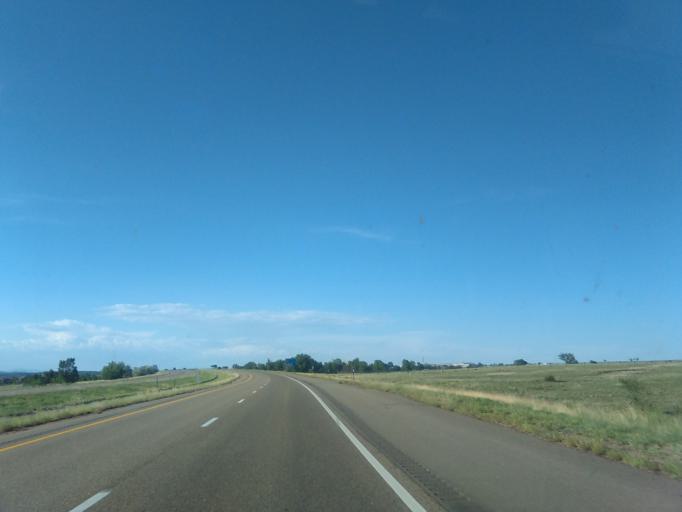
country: US
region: New Mexico
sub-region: San Miguel County
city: Las Vegas
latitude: 35.6144
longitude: -105.2034
